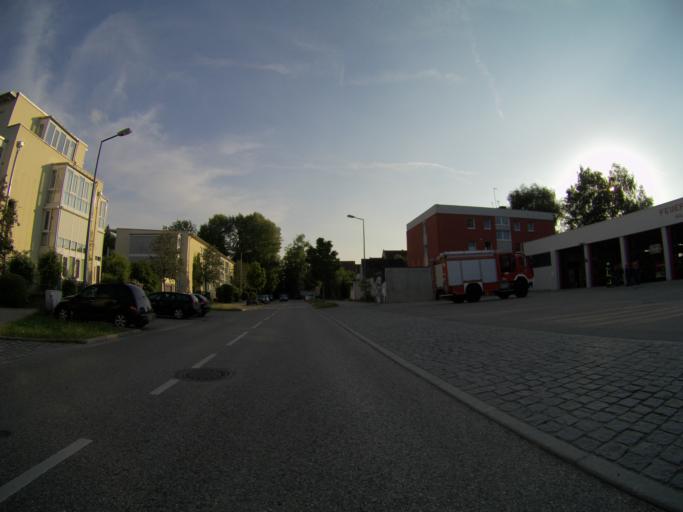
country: DE
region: Bavaria
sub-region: Upper Bavaria
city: Freising
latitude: 48.3895
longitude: 11.7659
